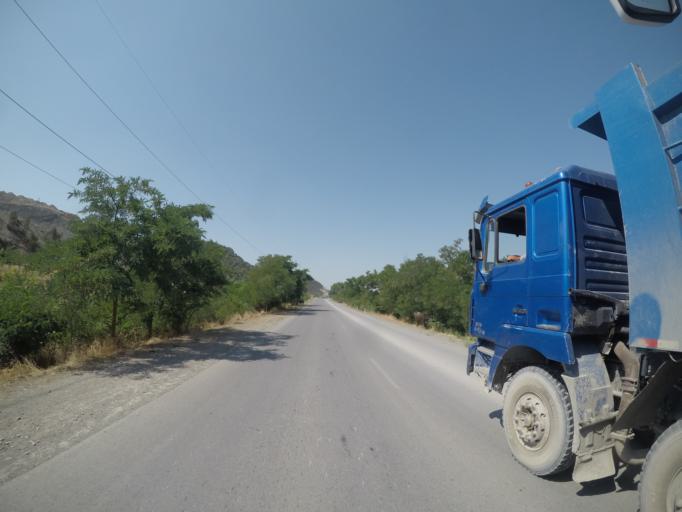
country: AZ
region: Agdas
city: Agdas
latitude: 40.7414
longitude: 47.5829
